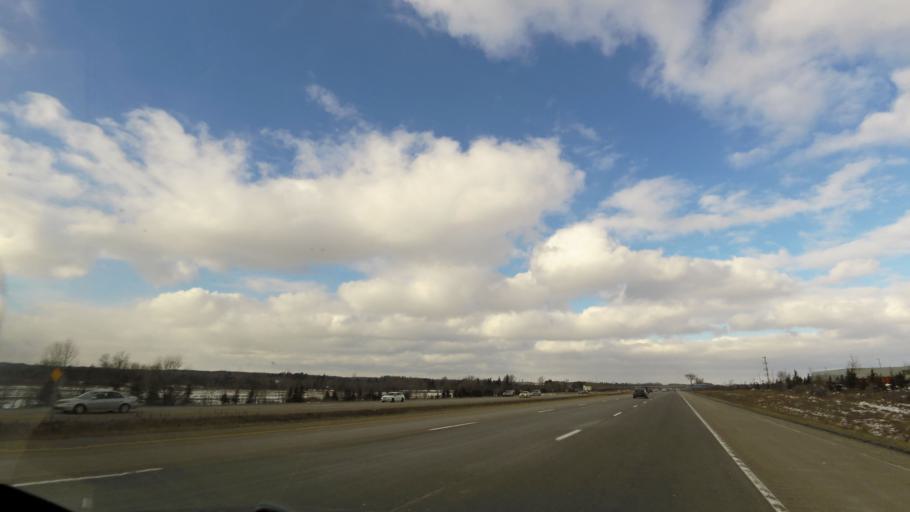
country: CA
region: Ontario
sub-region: York
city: Richmond Hill
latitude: 43.9120
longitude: -79.3866
